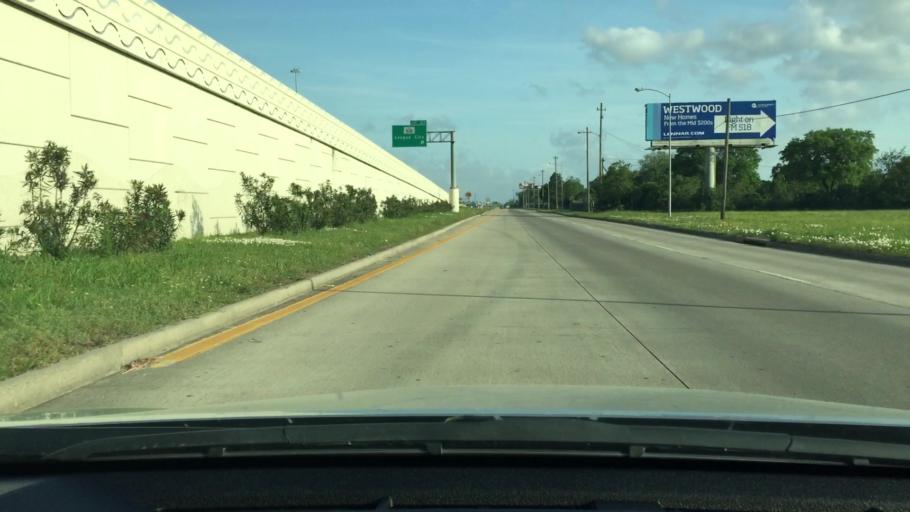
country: US
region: Texas
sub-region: Harris County
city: Webster
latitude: 29.5199
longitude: -95.1246
